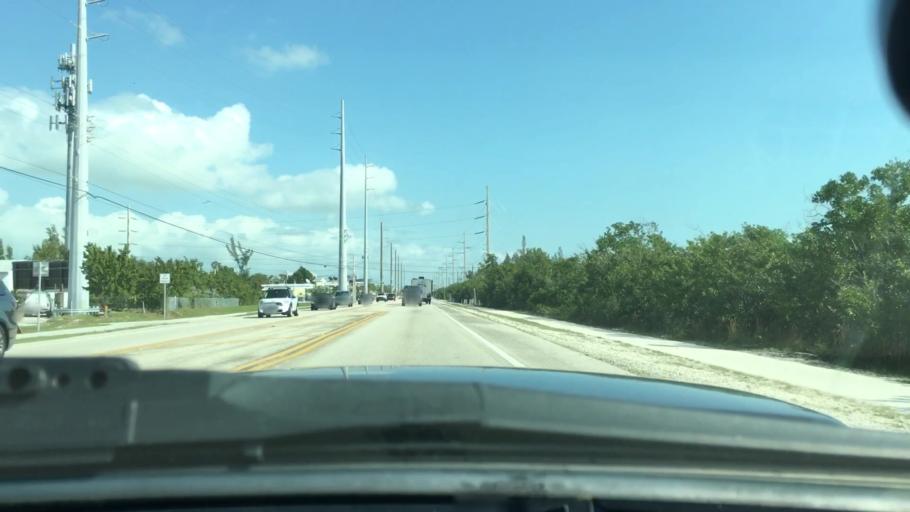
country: US
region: Florida
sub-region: Monroe County
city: Big Coppitt Key
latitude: 24.5951
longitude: -81.6609
